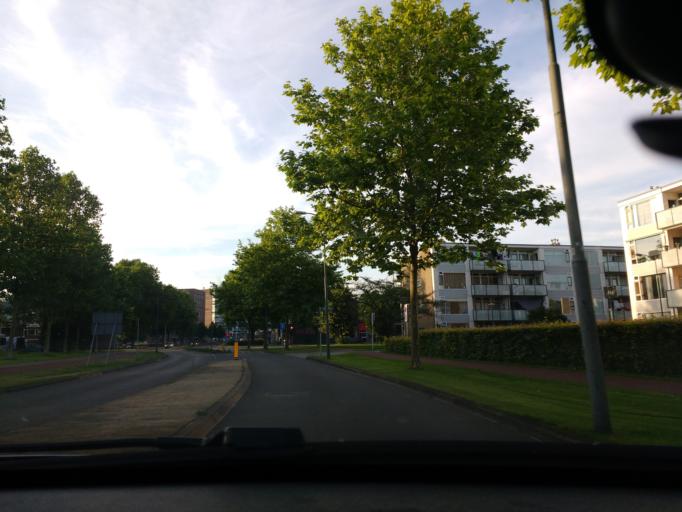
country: NL
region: Utrecht
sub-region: Gemeente Veenendaal
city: Veenendaal
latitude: 52.0237
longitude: 5.5631
